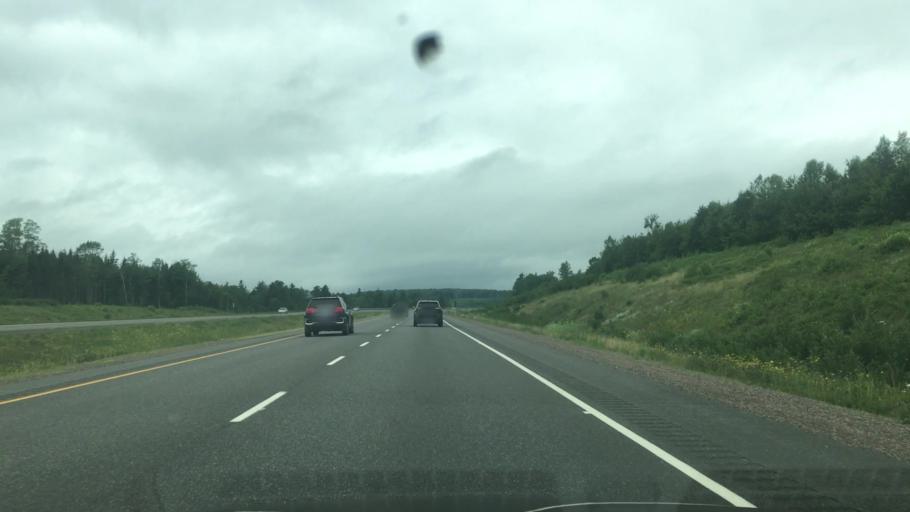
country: CA
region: Nova Scotia
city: Oxford
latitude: 45.4537
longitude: -63.6324
